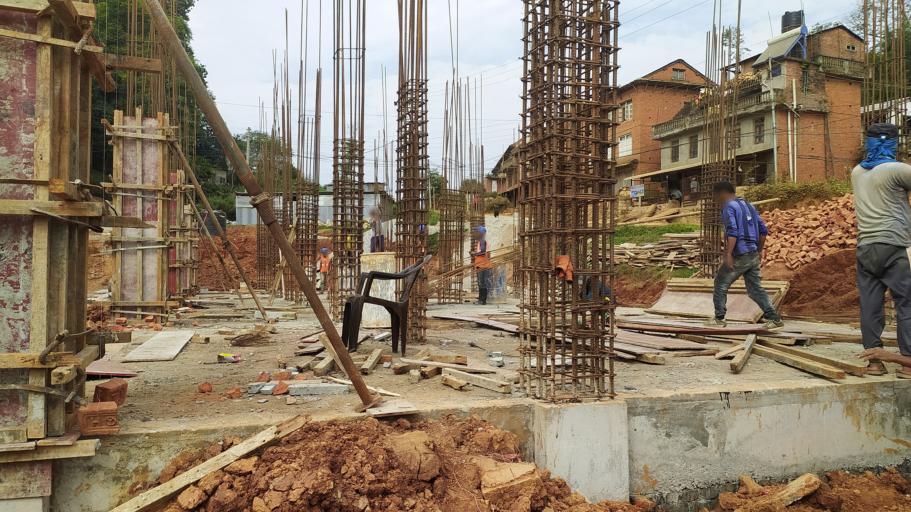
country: NP
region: Central Region
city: Panaoti
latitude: 27.5789
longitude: 85.5407
